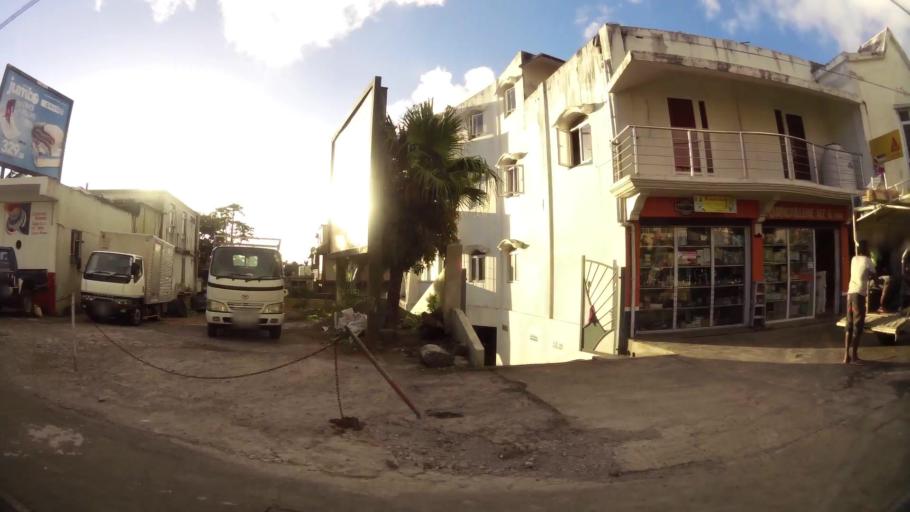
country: MU
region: Plaines Wilhems
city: Curepipe
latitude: -20.3052
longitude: 57.5309
